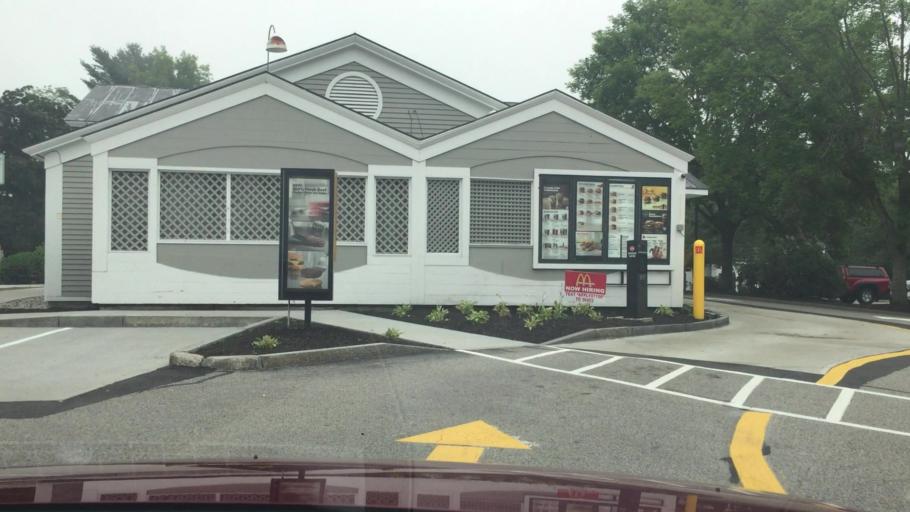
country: US
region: Maine
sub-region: Cumberland County
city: Freeport
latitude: 43.8605
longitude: -70.1021
